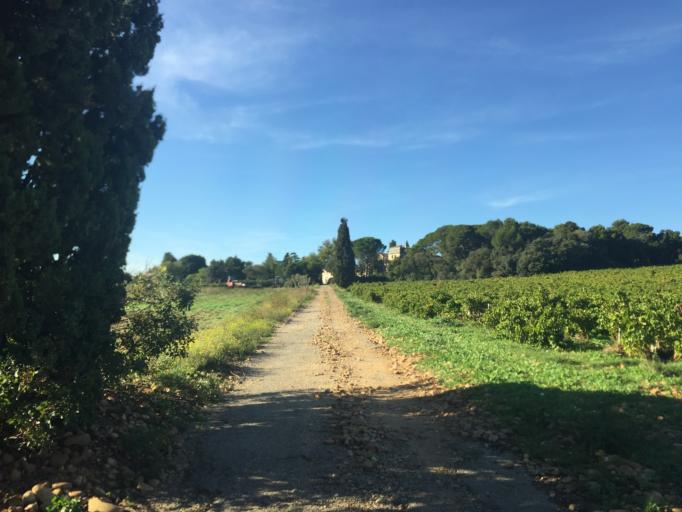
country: FR
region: Provence-Alpes-Cote d'Azur
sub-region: Departement du Vaucluse
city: Chateauneuf-du-Pape
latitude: 44.0499
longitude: 4.8405
